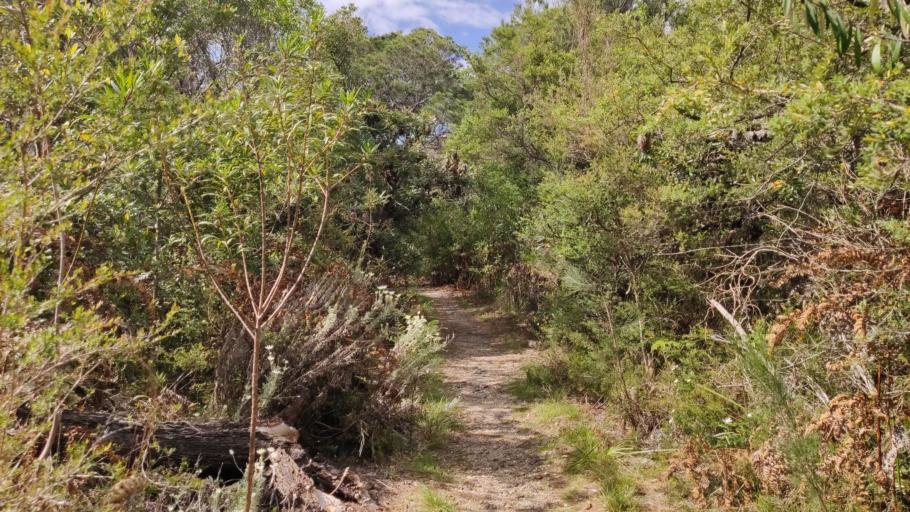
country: AU
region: New South Wales
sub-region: Port Macquarie-Hastings
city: North Haven
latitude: -31.6433
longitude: 152.8363
